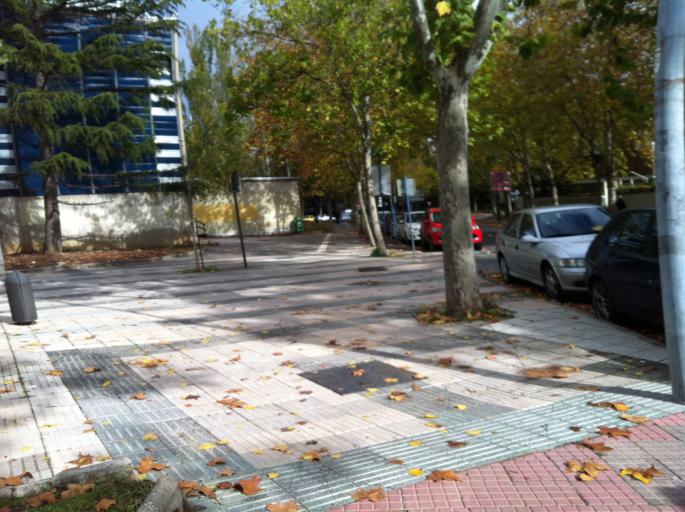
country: ES
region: Basque Country
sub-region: Provincia de Alava
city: Gasteiz / Vitoria
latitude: 42.8373
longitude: -2.6851
